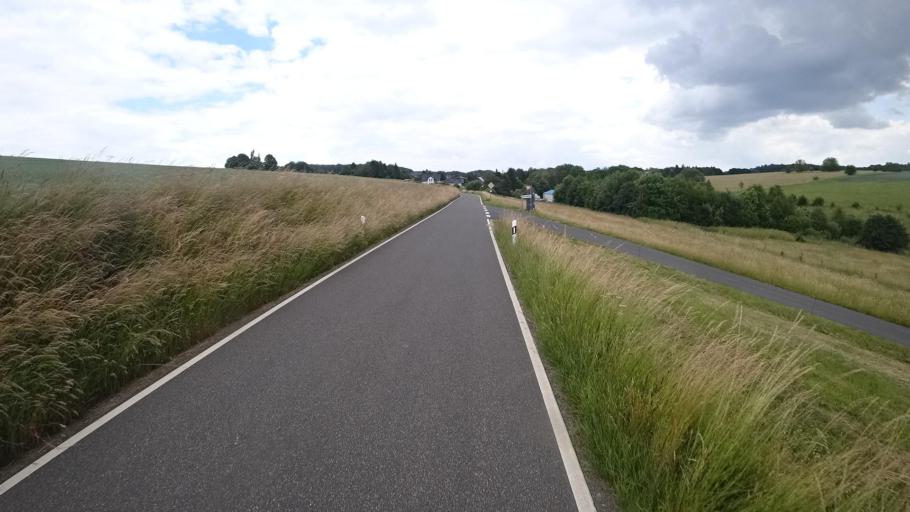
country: DE
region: Rheinland-Pfalz
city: Volkerzen
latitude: 50.7184
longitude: 7.6900
